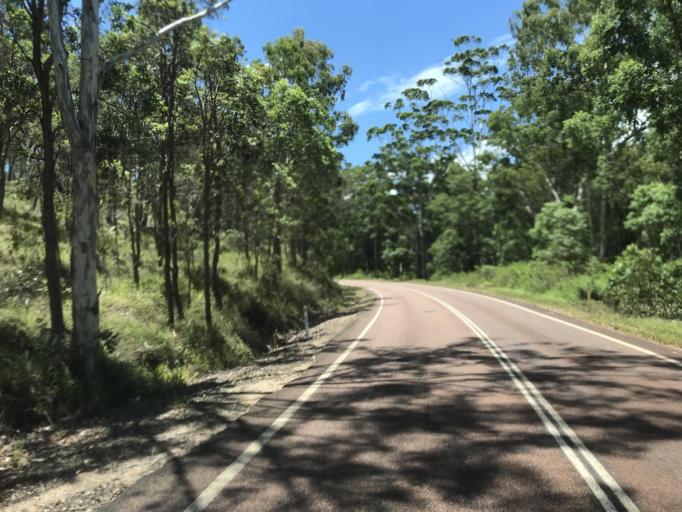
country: AU
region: Queensland
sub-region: Tablelands
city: Ravenshoe
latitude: -17.5898
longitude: 145.4733
